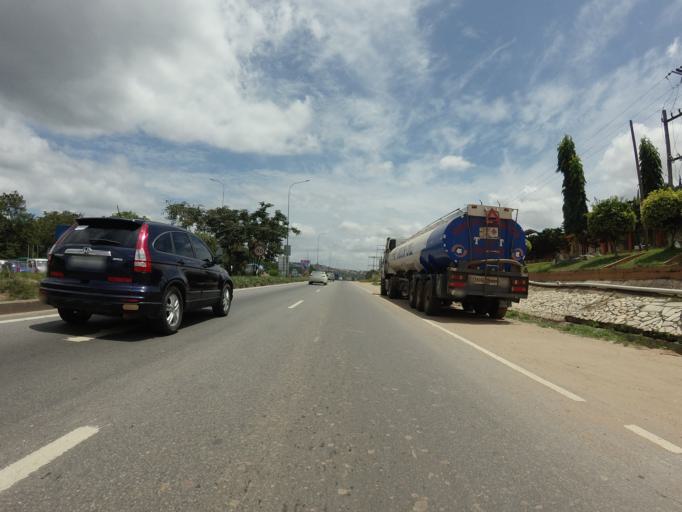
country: GH
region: Central
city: Kasoa
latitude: 5.5485
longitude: -0.3786
